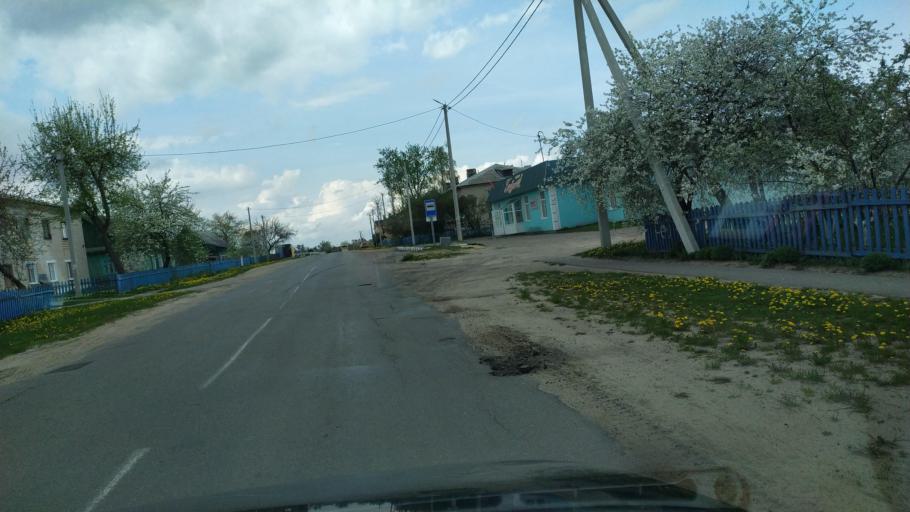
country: BY
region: Brest
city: Pruzhany
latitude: 52.5659
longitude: 24.4193
